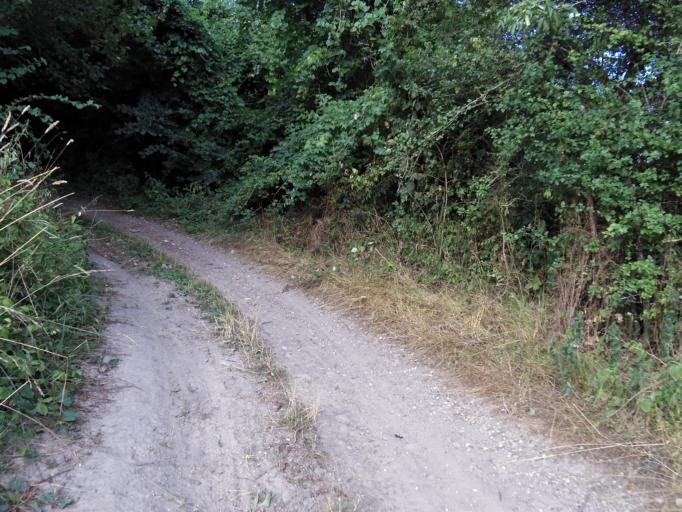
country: FR
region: Rhone-Alpes
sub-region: Departement de l'Ain
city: Perouges
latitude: 45.9176
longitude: 5.1813
